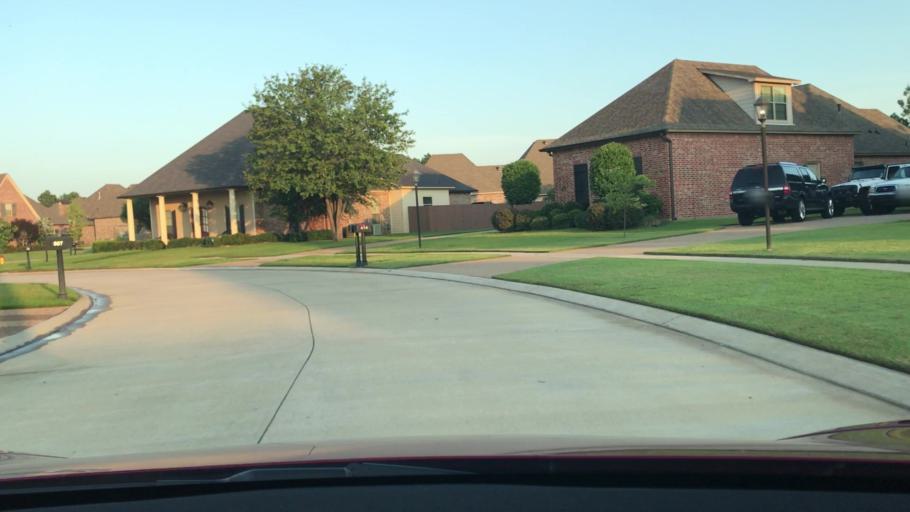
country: US
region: Louisiana
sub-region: Bossier Parish
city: Bossier City
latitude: 32.3937
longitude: -93.7035
